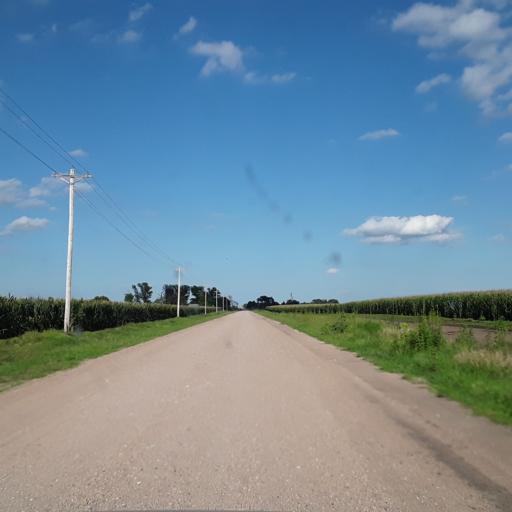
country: US
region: Nebraska
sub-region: Hall County
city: Wood River
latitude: 40.9167
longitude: -98.5693
